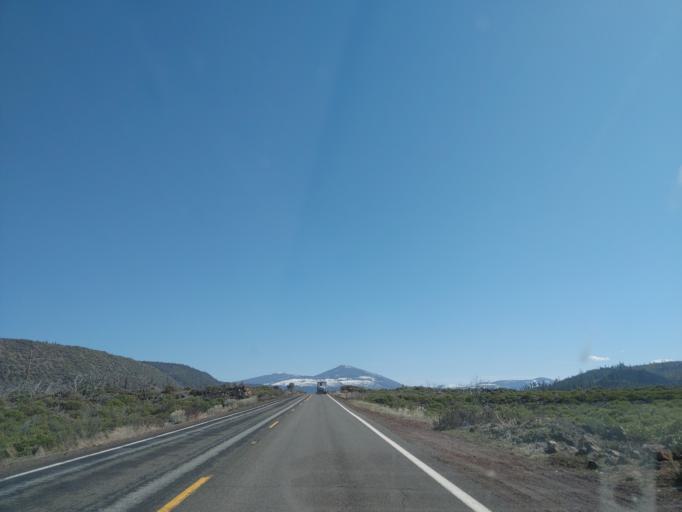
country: US
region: California
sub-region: Shasta County
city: Burney
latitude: 40.7161
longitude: -121.4233
